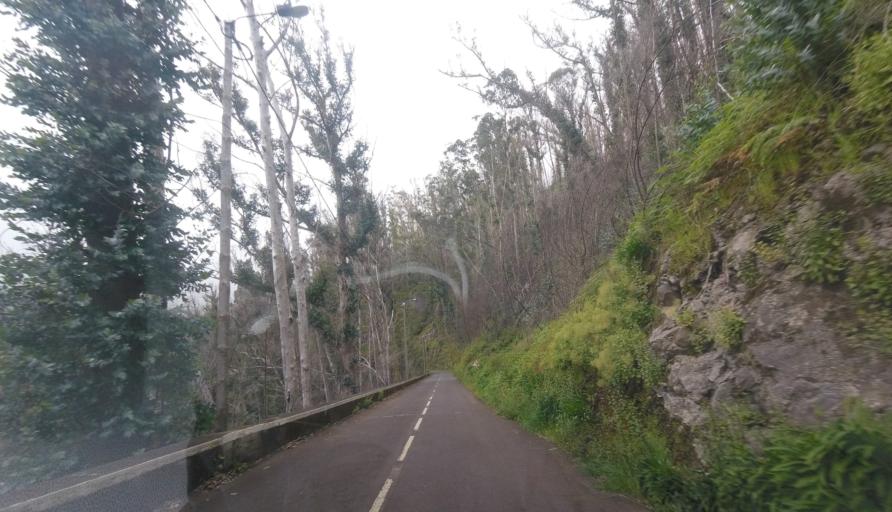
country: PT
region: Madeira
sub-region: Funchal
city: Nossa Senhora do Monte
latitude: 32.6818
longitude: -16.8909
